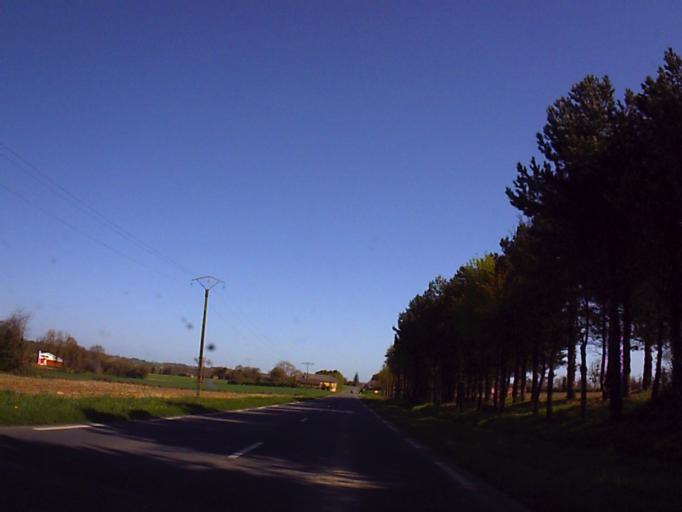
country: FR
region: Brittany
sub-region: Departement d'Ille-et-Vilaine
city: Quedillac
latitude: 48.2269
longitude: -2.1767
